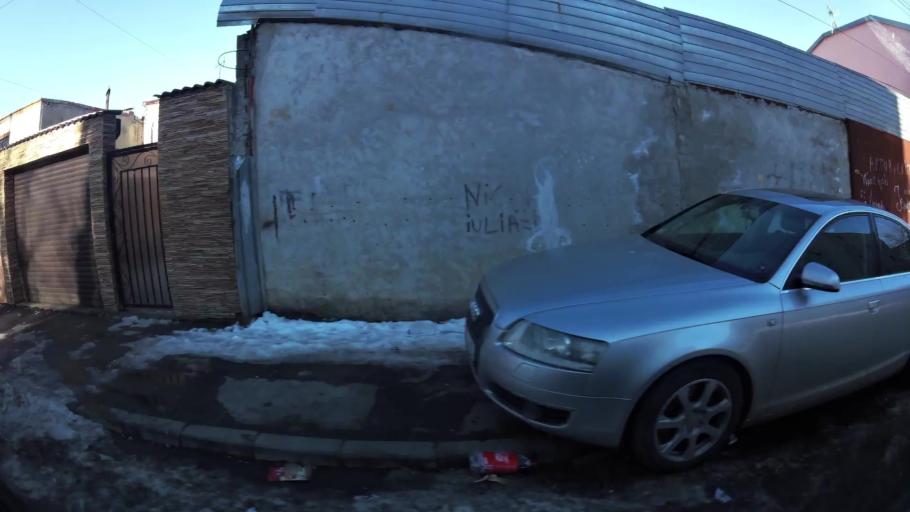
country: RO
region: Bucuresti
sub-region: Municipiul Bucuresti
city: Bucuresti
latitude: 44.4016
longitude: 26.0878
